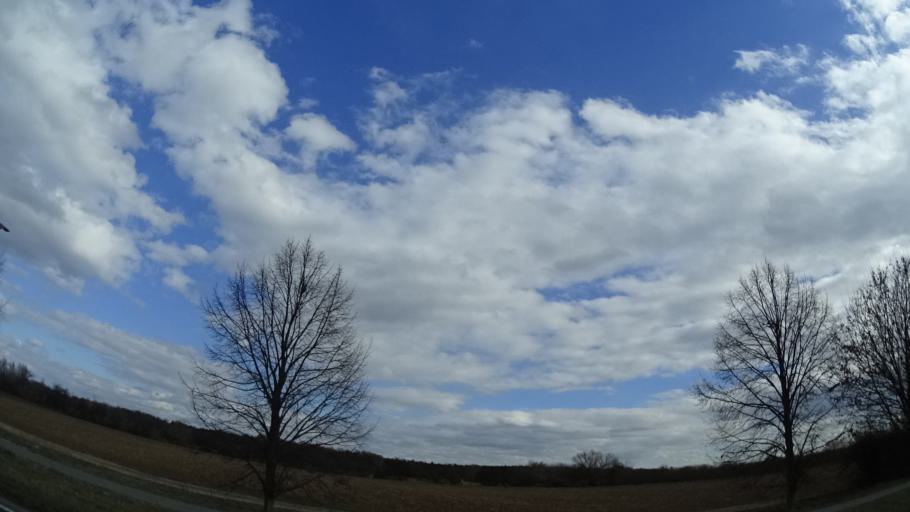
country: DE
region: Hesse
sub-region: Regierungsbezirk Darmstadt
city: Gross-Gerau
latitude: 49.8902
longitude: 8.4801
